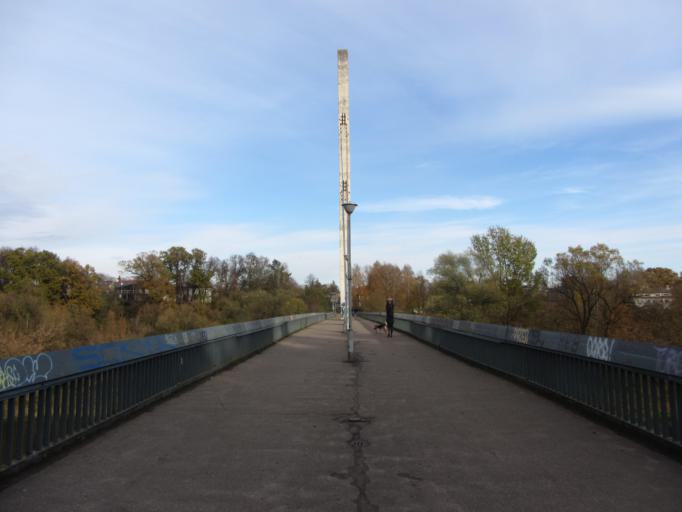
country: LT
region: Vilnius County
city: Seskine
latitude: 54.6912
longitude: 25.2419
